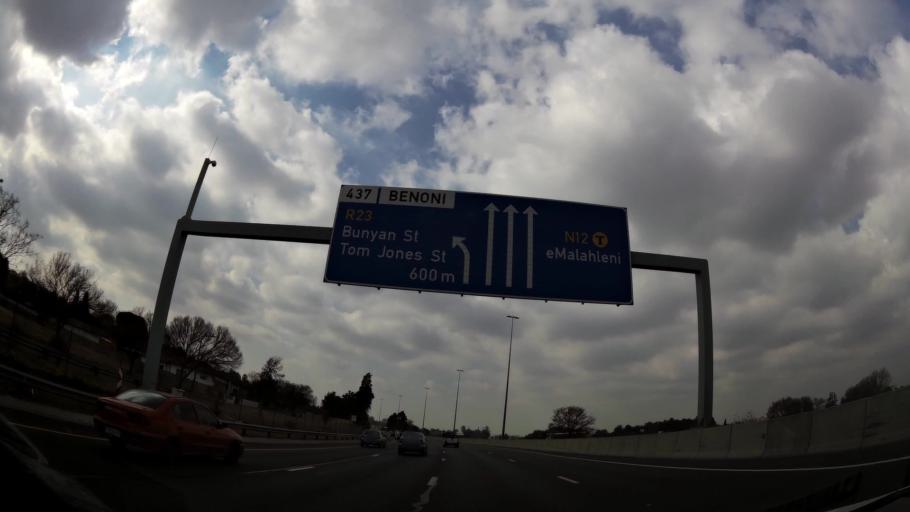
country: ZA
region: Gauteng
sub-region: Ekurhuleni Metropolitan Municipality
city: Benoni
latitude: -26.1807
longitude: 28.3011
